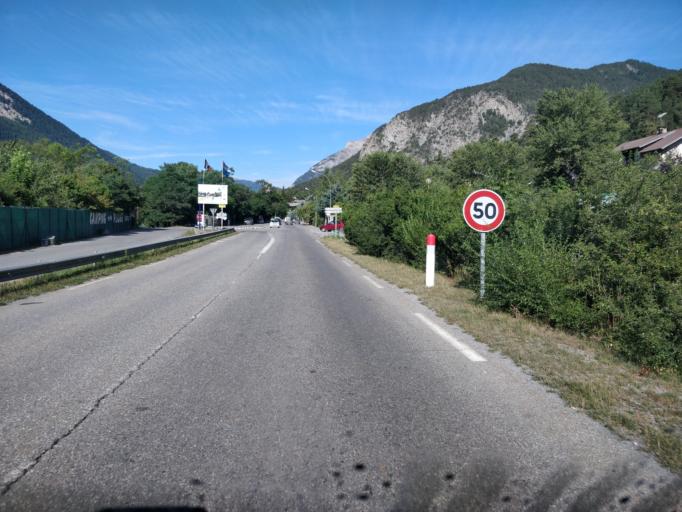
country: FR
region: Provence-Alpes-Cote d'Azur
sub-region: Departement des Alpes-de-Haute-Provence
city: Barcelonnette
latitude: 44.3931
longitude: 6.5752
